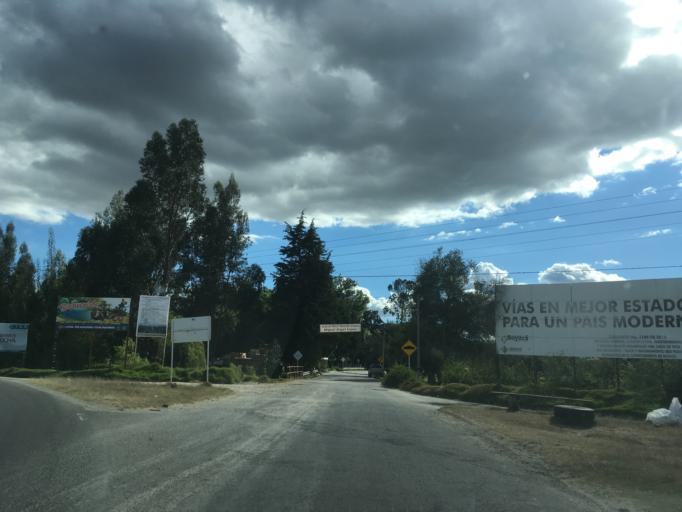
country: CO
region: Boyaca
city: Firavitoba
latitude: 5.6445
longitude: -72.9895
